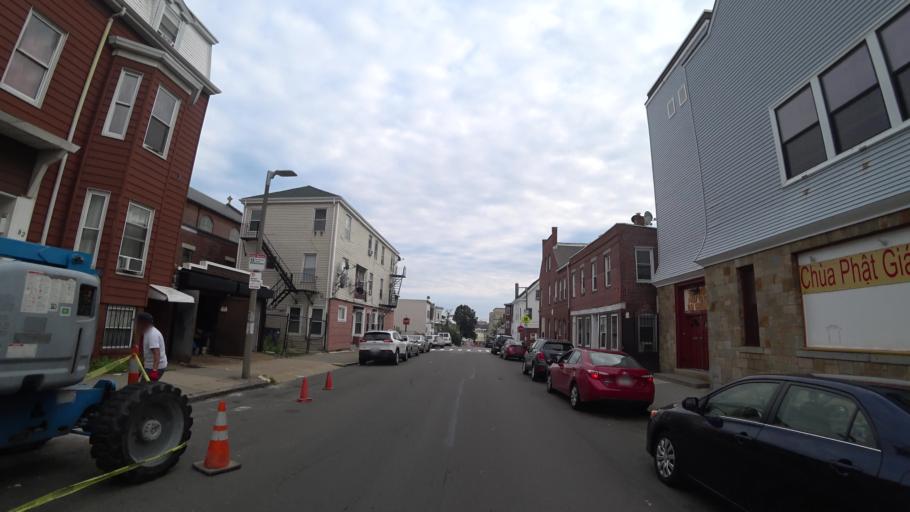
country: US
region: Massachusetts
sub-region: Suffolk County
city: Chelsea
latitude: 42.3784
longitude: -71.0374
